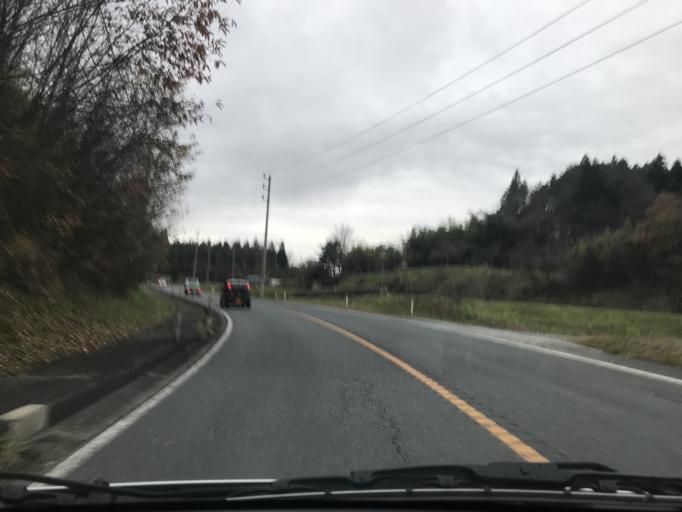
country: JP
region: Iwate
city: Ichinoseki
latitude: 39.0137
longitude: 141.3283
